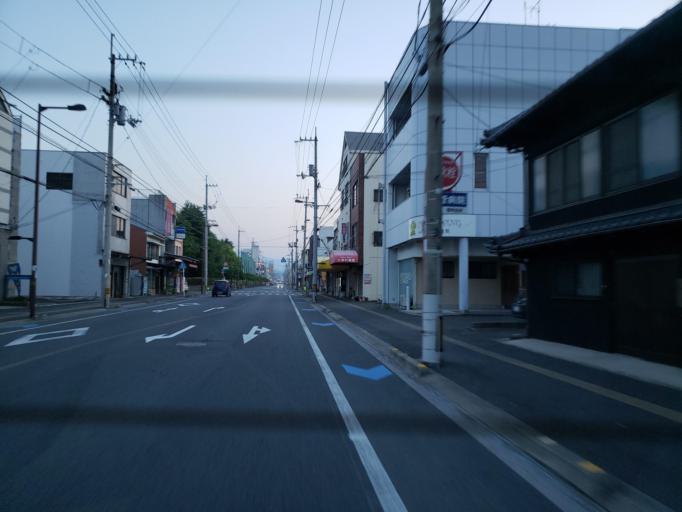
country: JP
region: Ehime
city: Hojo
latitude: 34.0571
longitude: 132.9898
